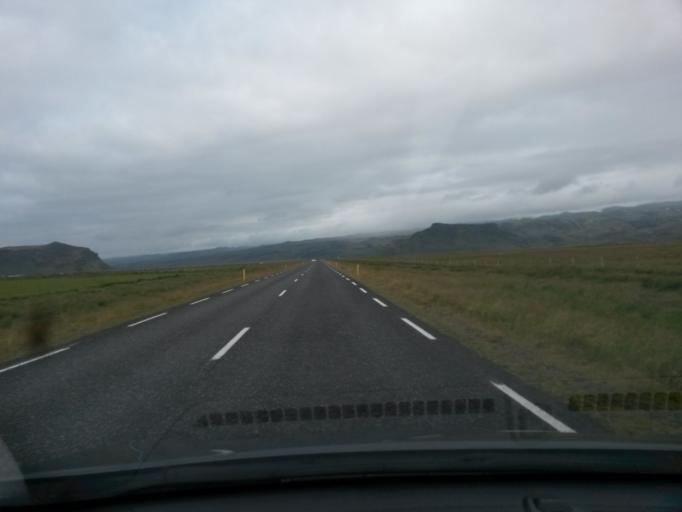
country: IS
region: South
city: Vestmannaeyjar
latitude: 63.4422
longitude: -19.1987
